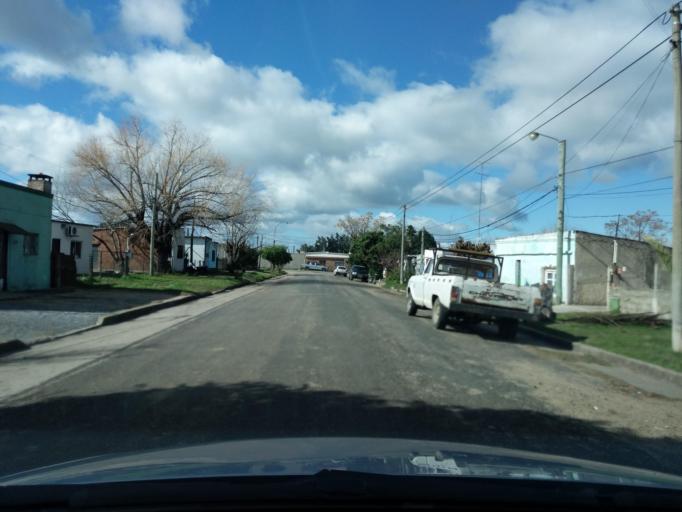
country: UY
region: Florida
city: Florida
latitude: -34.0812
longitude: -56.2201
